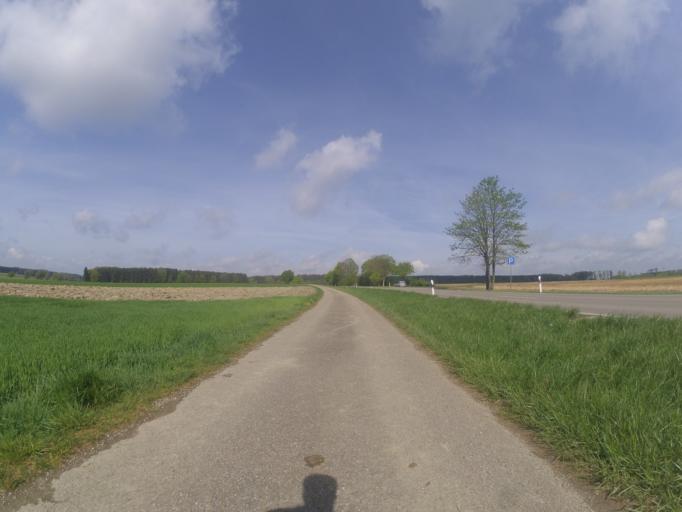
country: DE
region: Baden-Wuerttemberg
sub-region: Tuebingen Region
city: Griesingen
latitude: 48.2403
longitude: 9.8138
